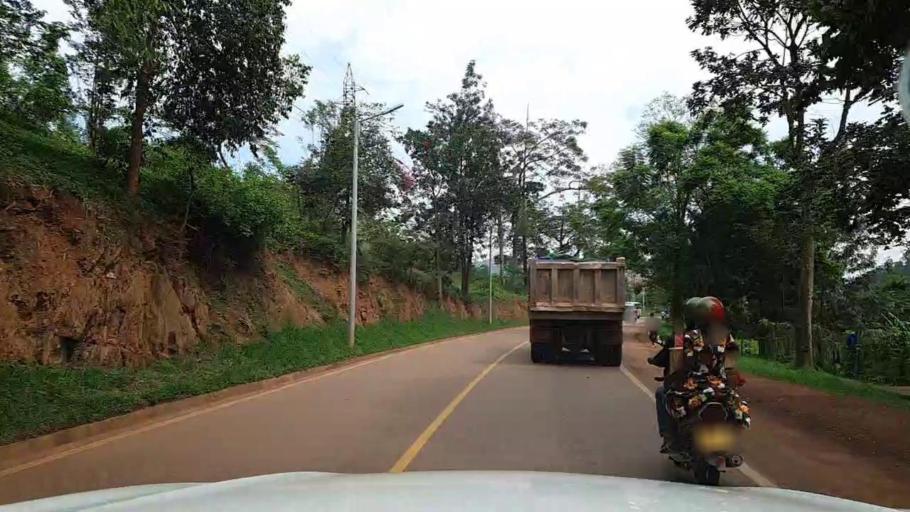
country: RW
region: Kigali
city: Kigali
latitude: -1.9156
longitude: 30.0473
